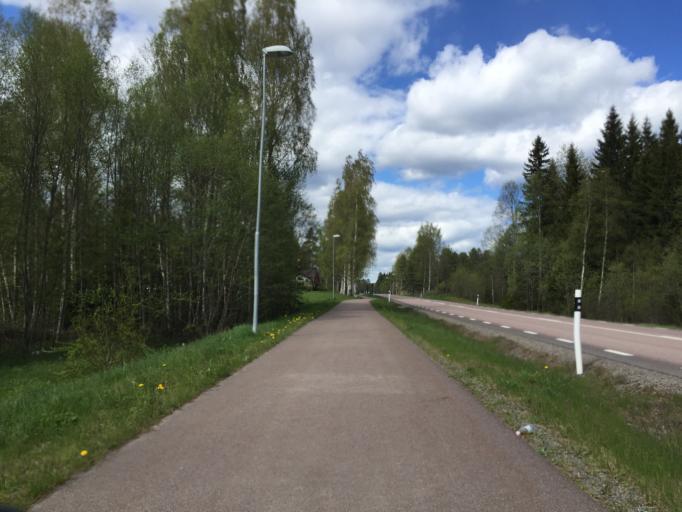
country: SE
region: Dalarna
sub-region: Ludvika Kommun
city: Ludvika
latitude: 60.2094
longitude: 15.2233
